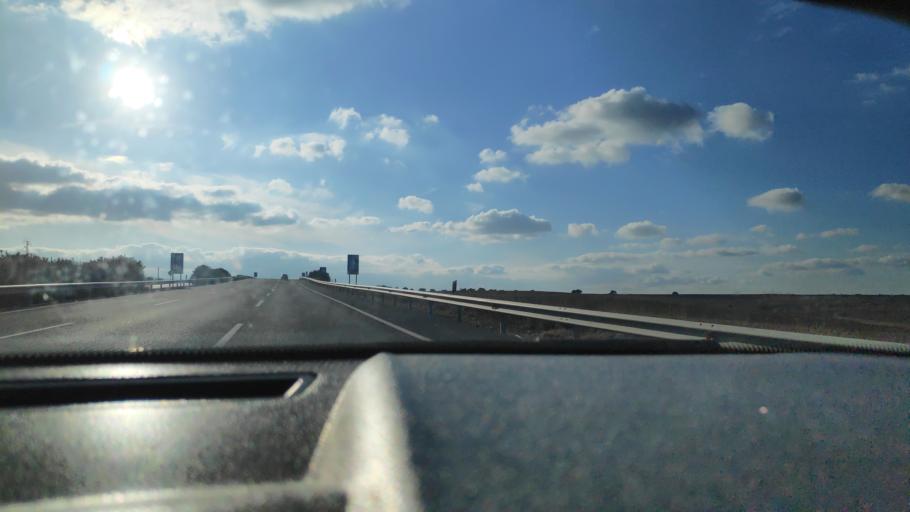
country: ES
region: Andalusia
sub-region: Provincia de Sevilla
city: La Luisiana
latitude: 37.5268
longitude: -5.3017
